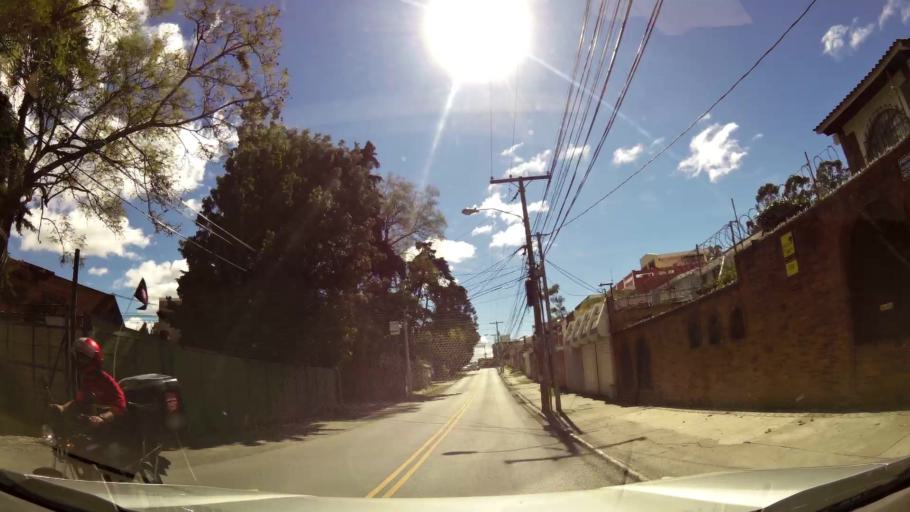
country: GT
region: Guatemala
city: Guatemala City
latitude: 14.6127
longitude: -90.4986
